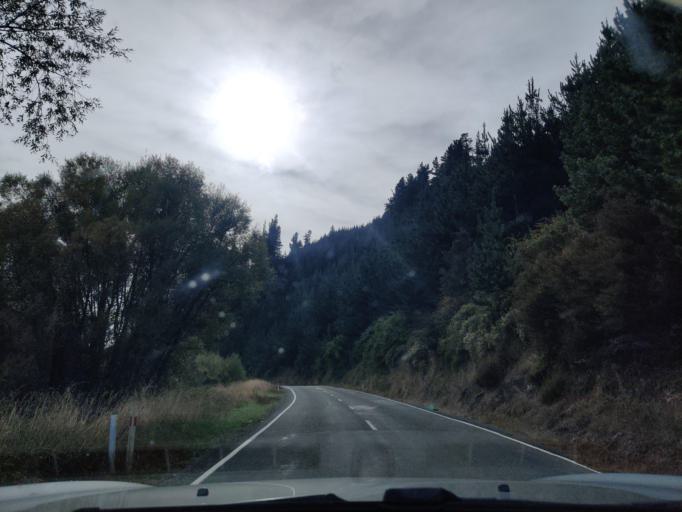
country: NZ
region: Tasman
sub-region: Tasman District
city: Wakefield
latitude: -41.7178
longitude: 173.1051
